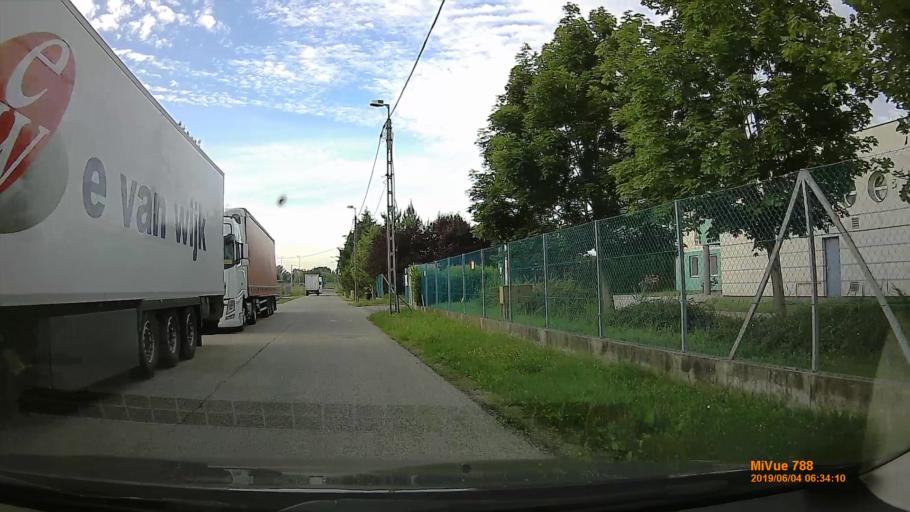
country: HU
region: Pest
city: Diosd
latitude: 47.3899
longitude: 18.9675
